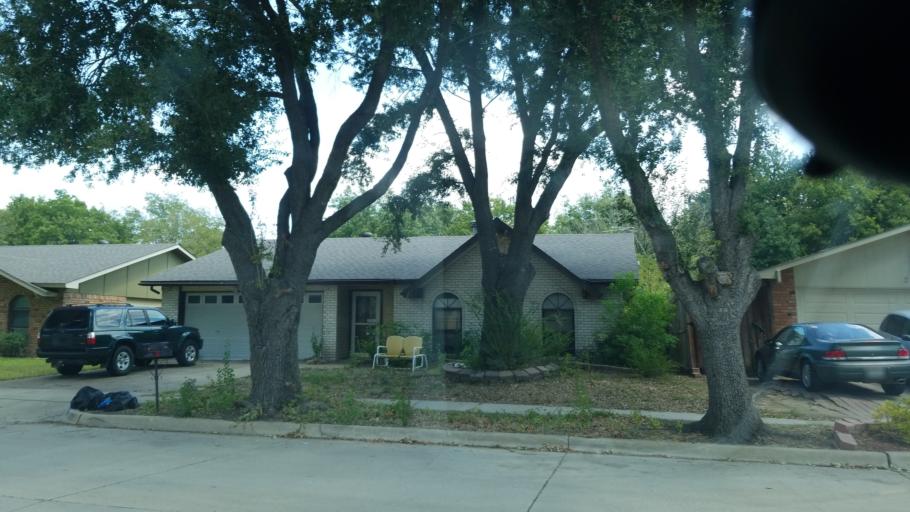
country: US
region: Texas
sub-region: Dallas County
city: Grand Prairie
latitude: 32.7067
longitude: -96.9989
